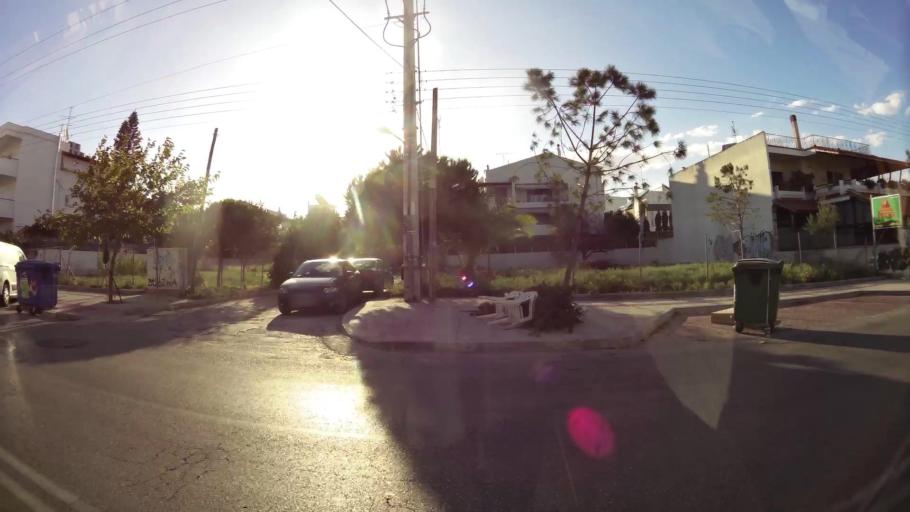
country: GR
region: Attica
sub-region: Nomarchia Athinas
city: Elliniko
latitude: 37.8820
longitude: 23.7445
